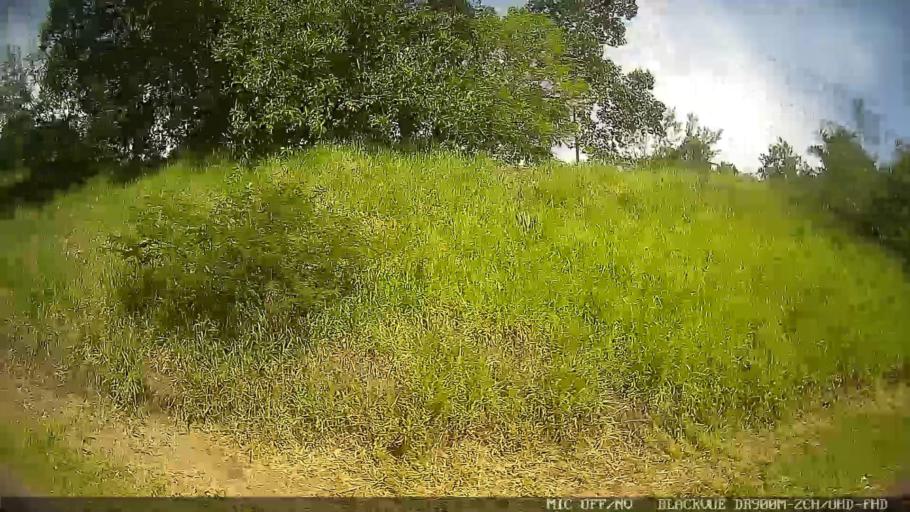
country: BR
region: Sao Paulo
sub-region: Tiete
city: Tiete
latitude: -23.1065
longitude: -47.6942
